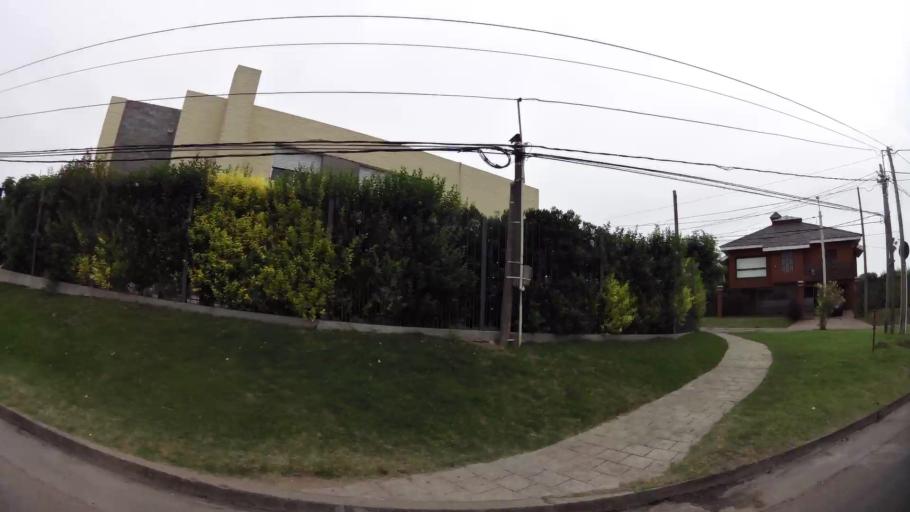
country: UY
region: Canelones
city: Las Piedras
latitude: -34.7332
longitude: -56.2155
